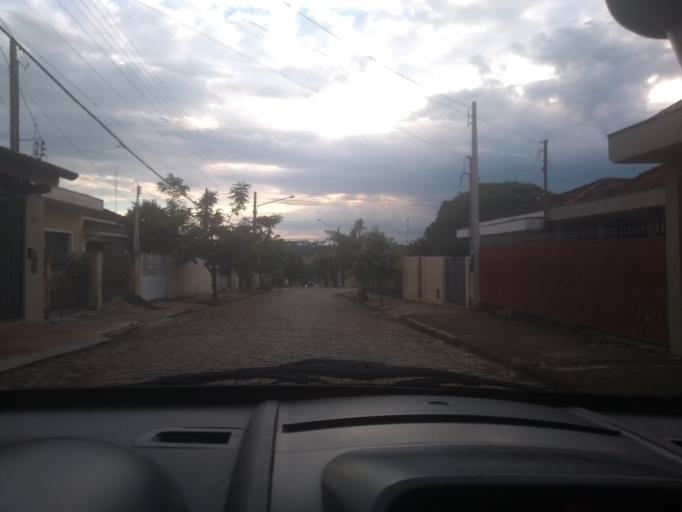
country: BR
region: Sao Paulo
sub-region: Casa Branca
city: Casa Branca
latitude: -21.7780
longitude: -47.0838
